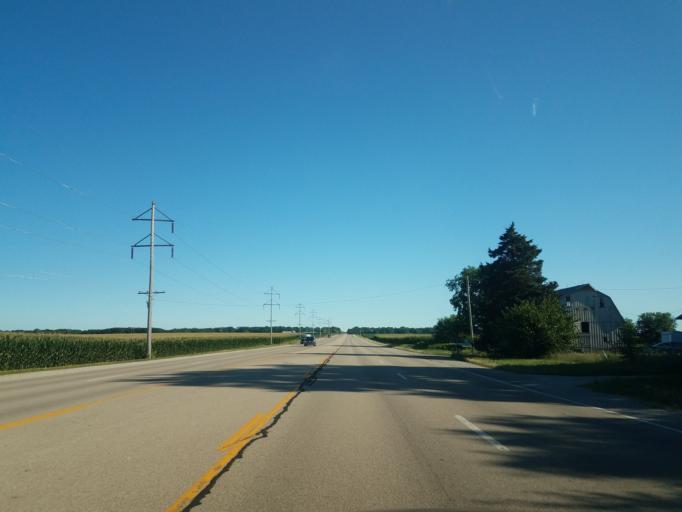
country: US
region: Illinois
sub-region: McLean County
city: Downs
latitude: 40.4396
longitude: -88.9017
